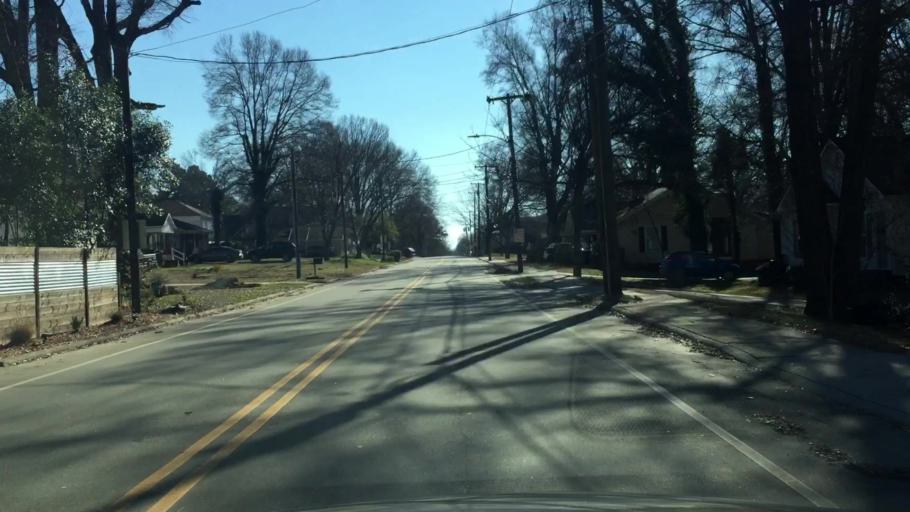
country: US
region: North Carolina
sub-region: Iredell County
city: Mooresville
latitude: 35.5823
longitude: -80.8007
